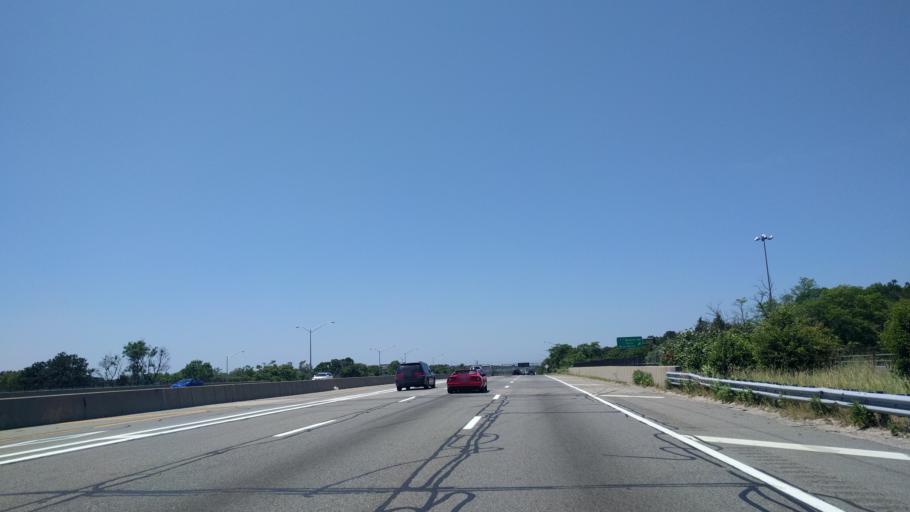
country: US
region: New York
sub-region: Suffolk County
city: Holtsville
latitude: 40.8204
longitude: -73.0533
